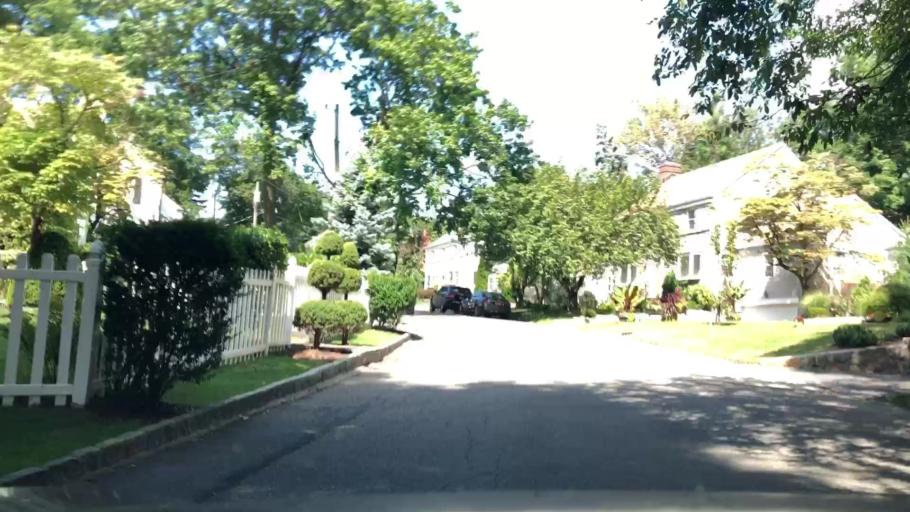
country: US
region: New York
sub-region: Westchester County
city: Pelham
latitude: 40.9284
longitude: -73.8144
